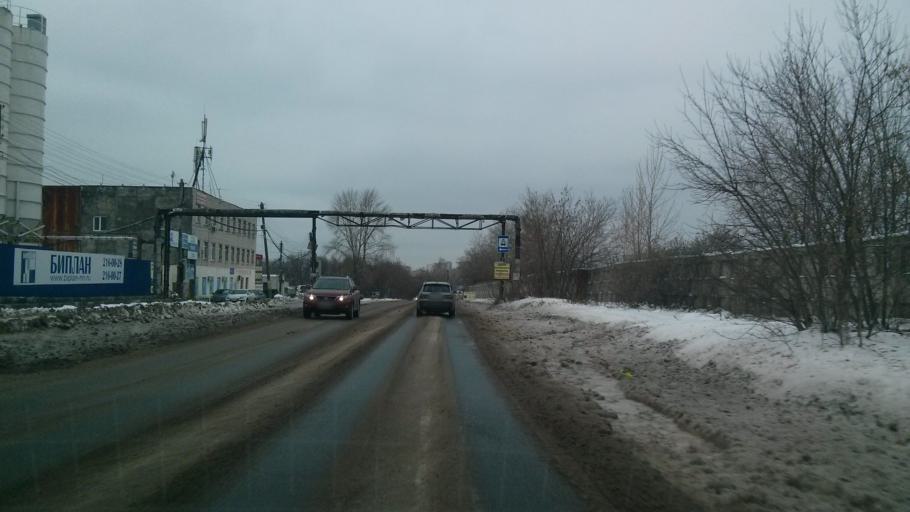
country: RU
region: Nizjnij Novgorod
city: Bor
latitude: 56.3073
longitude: 44.0568
